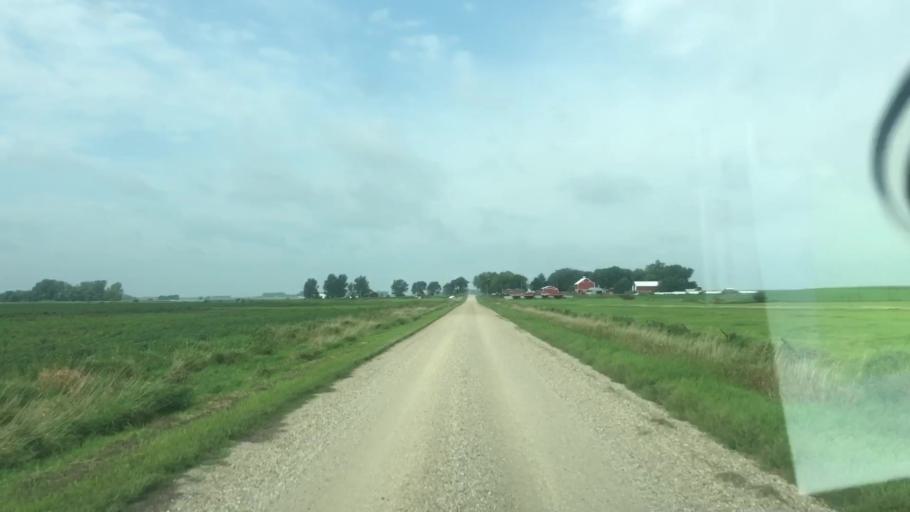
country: US
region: Iowa
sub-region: O'Brien County
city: Sheldon
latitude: 43.2725
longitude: -95.9122
